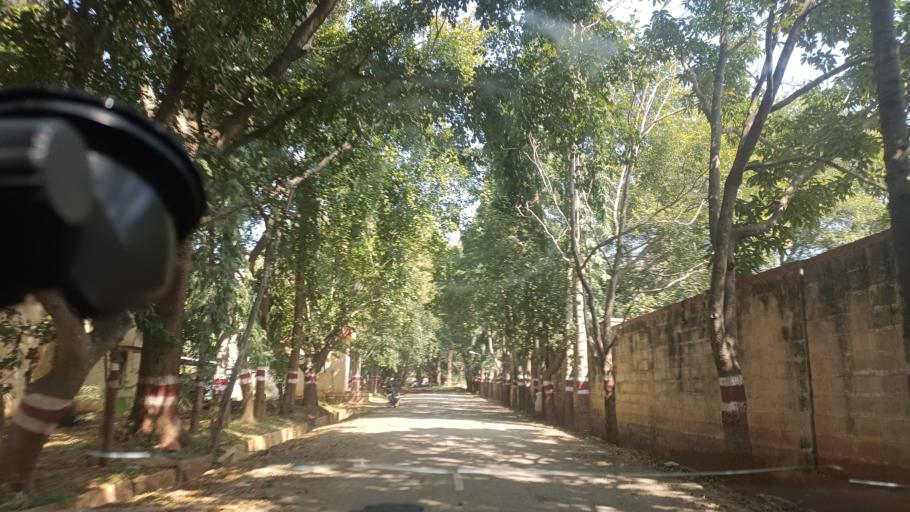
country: IN
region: Karnataka
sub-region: Bangalore Urban
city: Yelahanka
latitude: 13.1224
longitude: 77.6054
